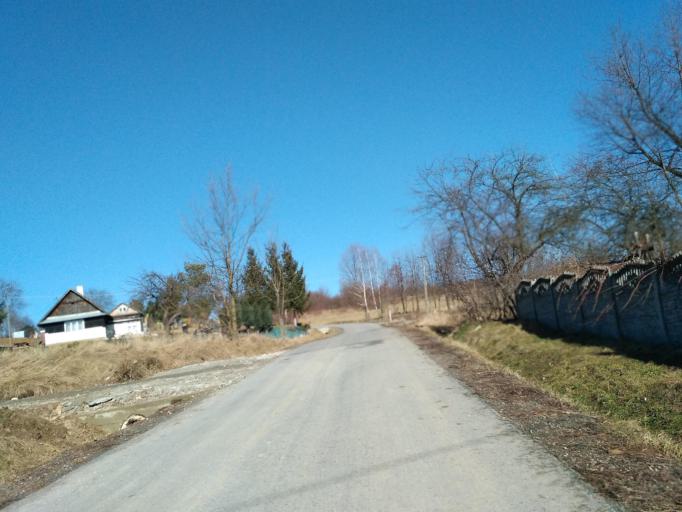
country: PL
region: Subcarpathian Voivodeship
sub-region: Powiat rzeszowski
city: Lubenia
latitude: 49.9321
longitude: 21.9460
